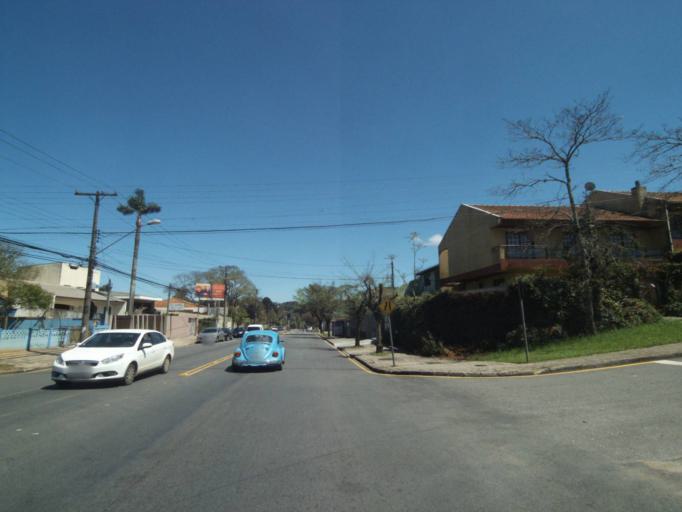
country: BR
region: Parana
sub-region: Curitiba
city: Curitiba
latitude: -25.3892
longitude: -49.2634
